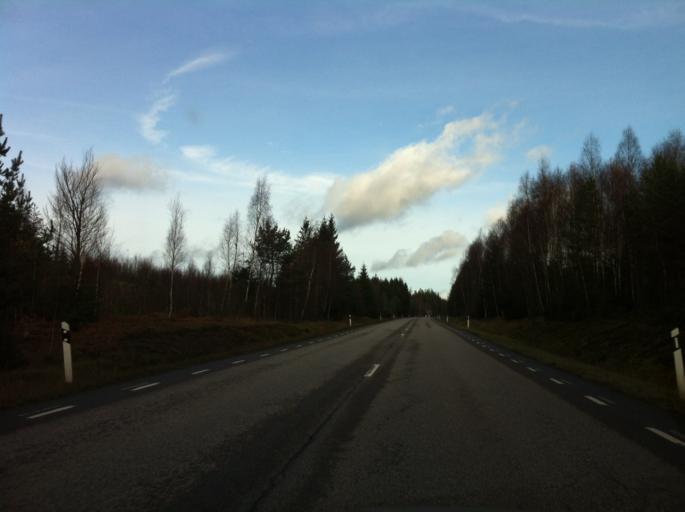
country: SE
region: Kronoberg
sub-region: Almhults Kommun
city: AElmhult
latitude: 56.5912
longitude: 14.1986
